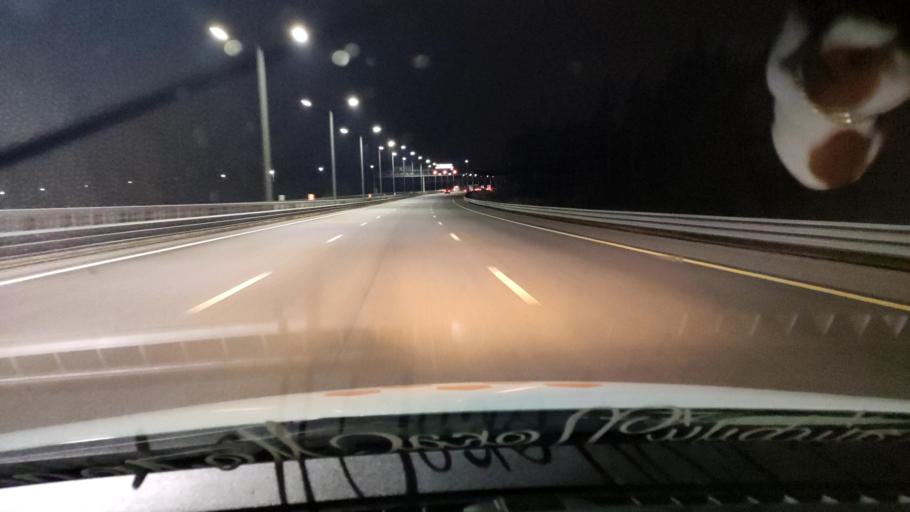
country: RU
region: Voronezj
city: Somovo
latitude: 51.7307
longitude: 39.3110
